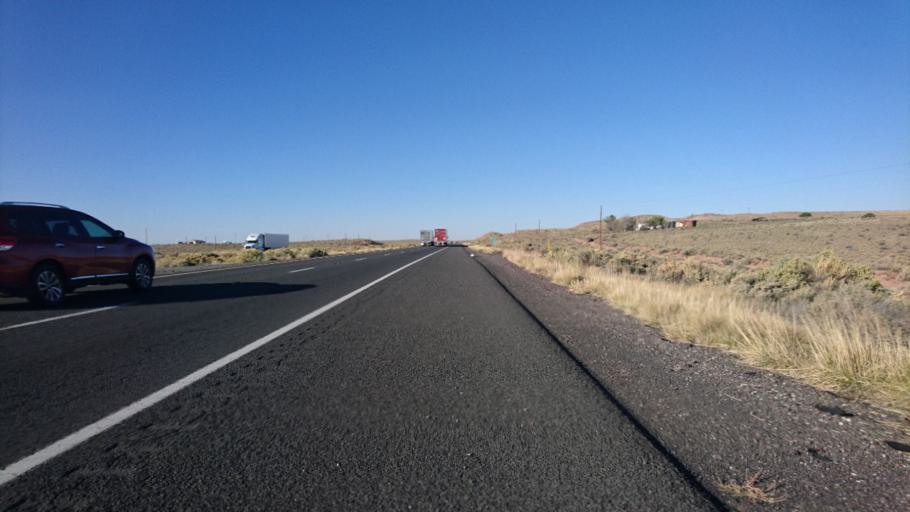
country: US
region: Arizona
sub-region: Apache County
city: Houck
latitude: 35.1173
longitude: -109.5738
